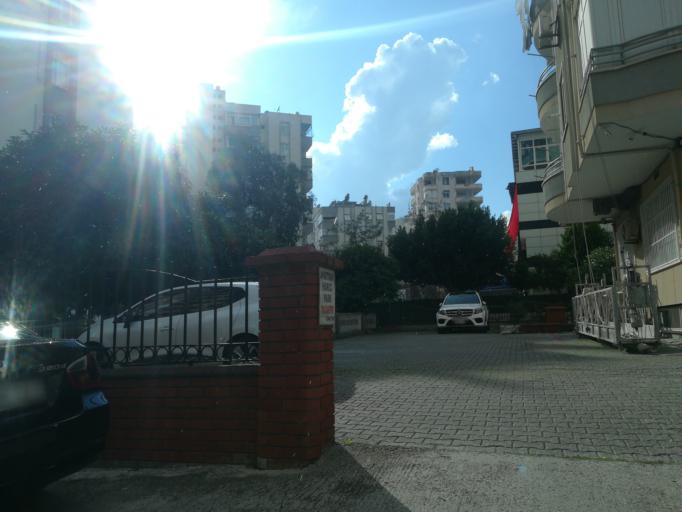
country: TR
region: Adana
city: Adana
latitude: 37.0454
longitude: 35.3029
